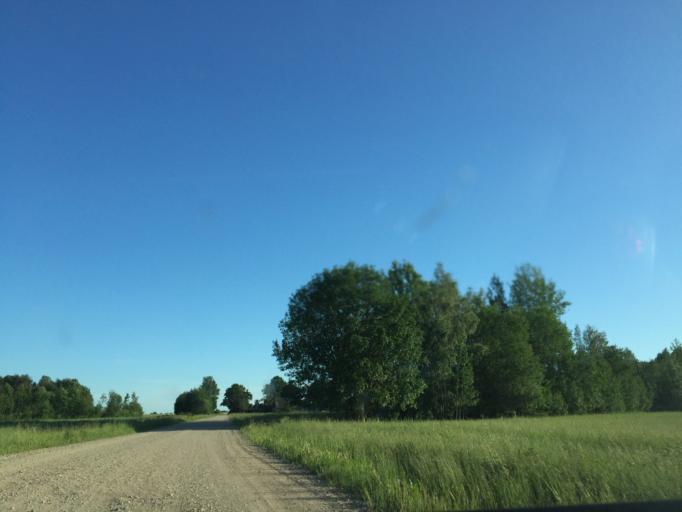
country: LV
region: Broceni
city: Broceni
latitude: 56.8388
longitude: 22.5660
